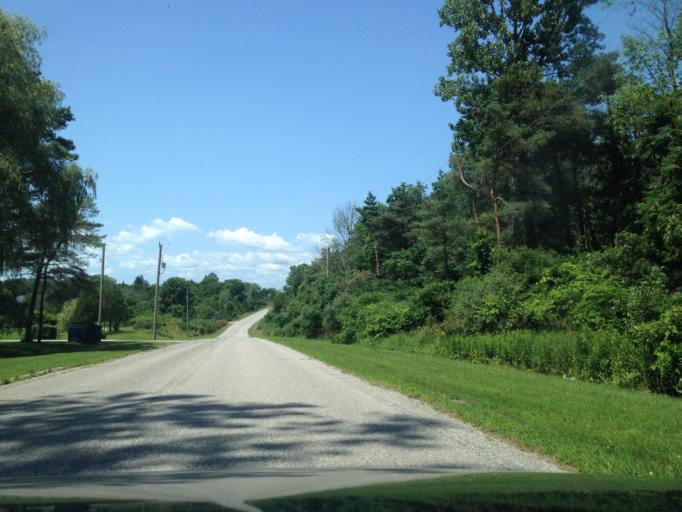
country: CA
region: Ontario
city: Aylmer
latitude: 42.6445
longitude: -80.7898
